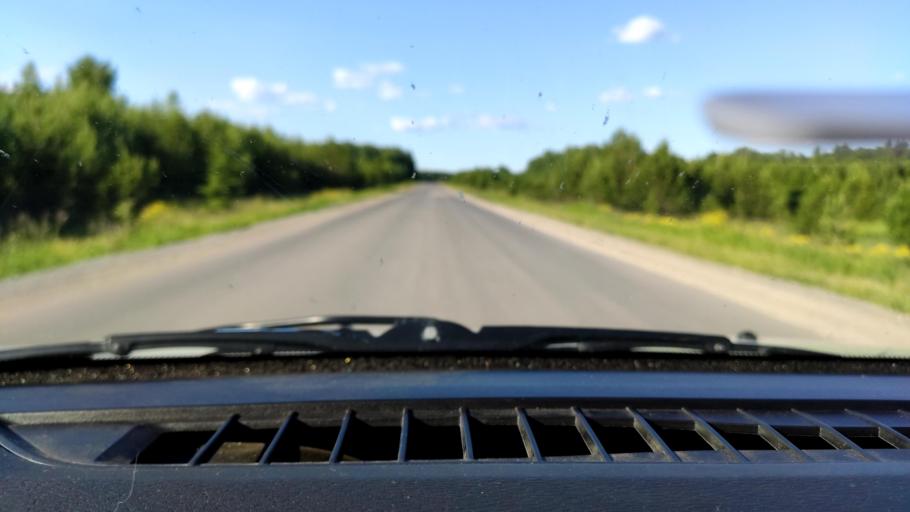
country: RU
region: Perm
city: Uinskoye
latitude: 57.1157
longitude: 56.6695
